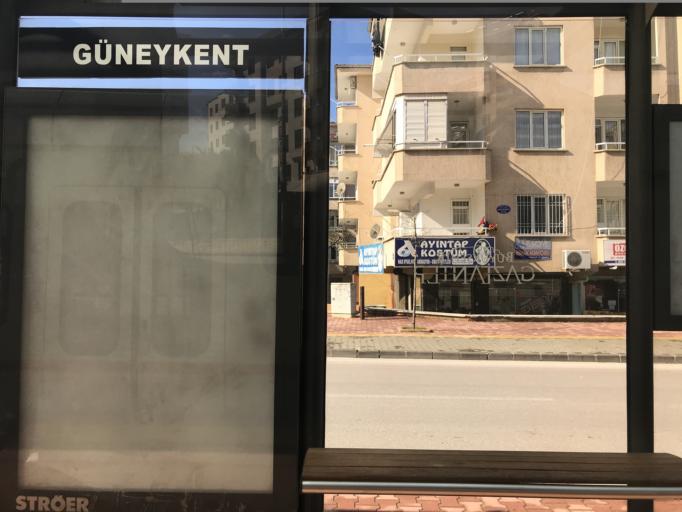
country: TR
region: Gaziantep
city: Sahinbey
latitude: 37.0297
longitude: 37.3268
